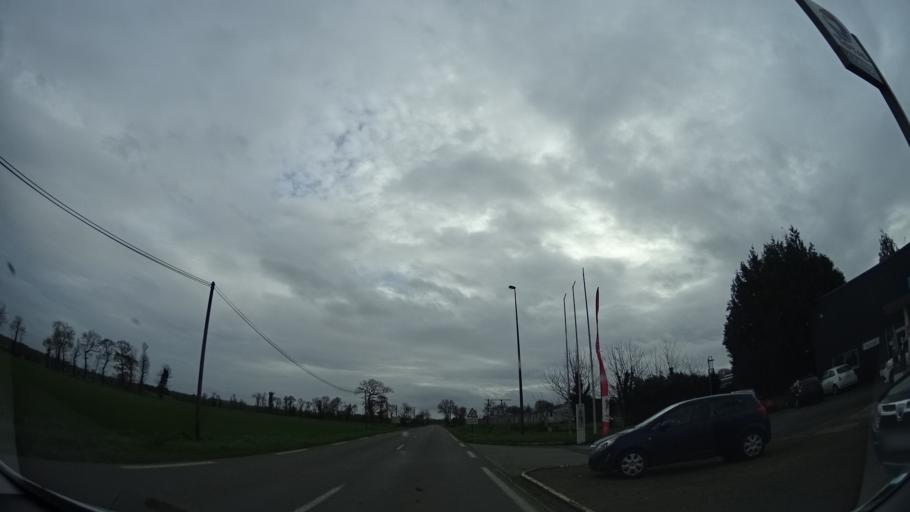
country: FR
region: Brittany
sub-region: Departement des Cotes-d'Armor
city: Evran
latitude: 48.3734
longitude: -1.9726
